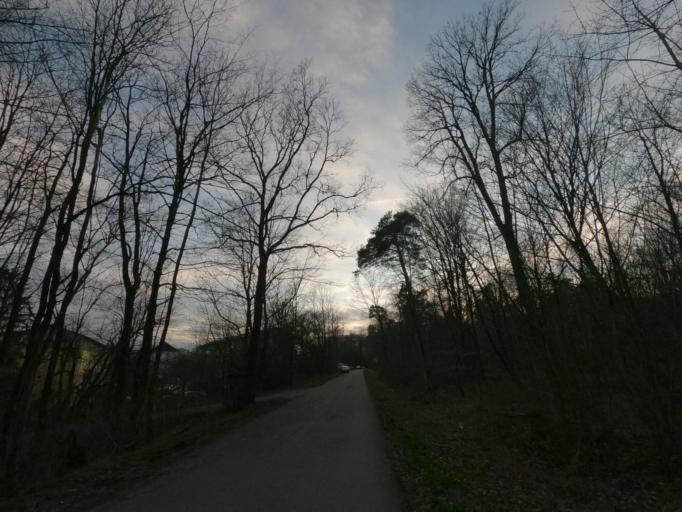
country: DE
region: Baden-Wuerttemberg
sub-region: Regierungsbezirk Stuttgart
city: Goeppingen
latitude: 48.7161
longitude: 9.6805
